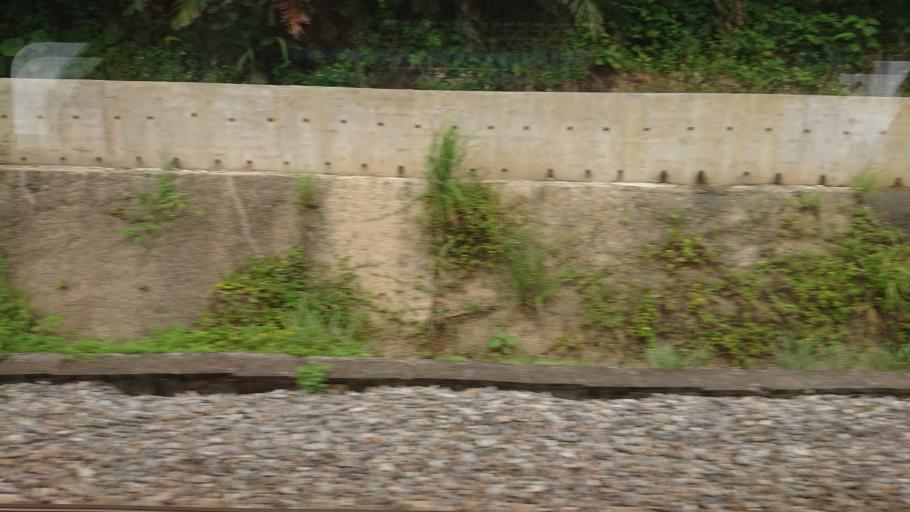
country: TW
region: Taiwan
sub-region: Keelung
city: Keelung
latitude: 24.9613
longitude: 121.9197
